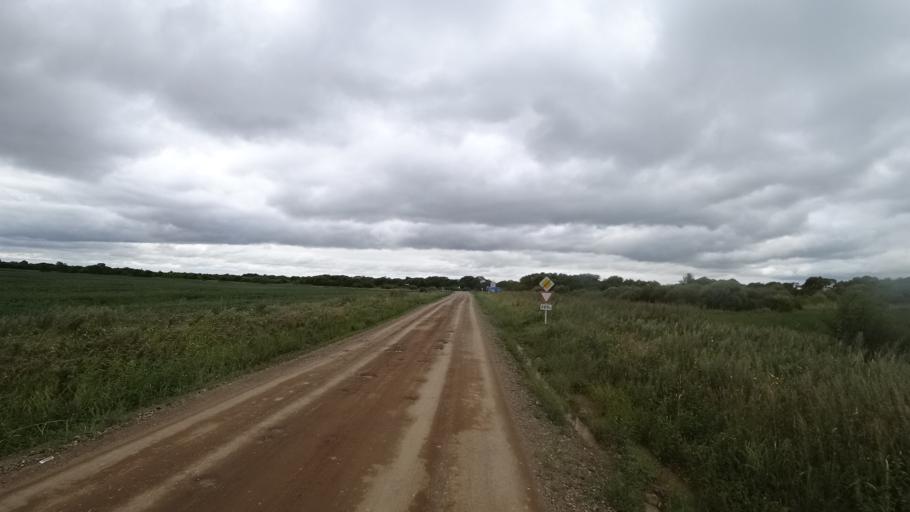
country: RU
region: Primorskiy
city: Chernigovka
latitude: 44.3447
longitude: 132.6086
